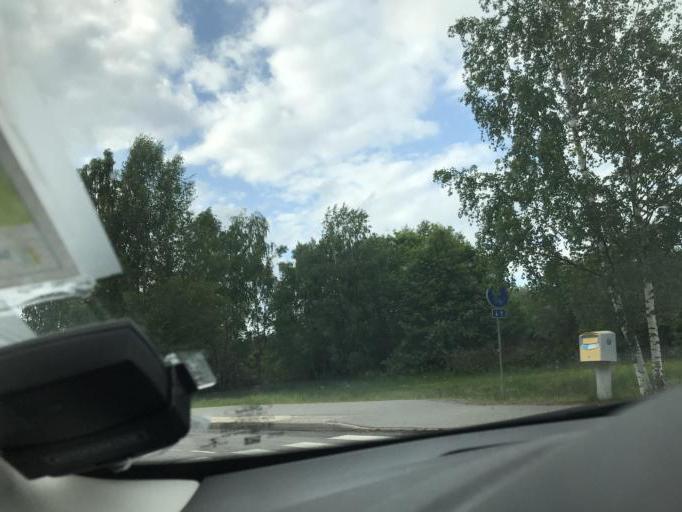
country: SE
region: Stockholm
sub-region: Botkyrka Kommun
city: Tumba
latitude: 59.1942
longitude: 17.8048
